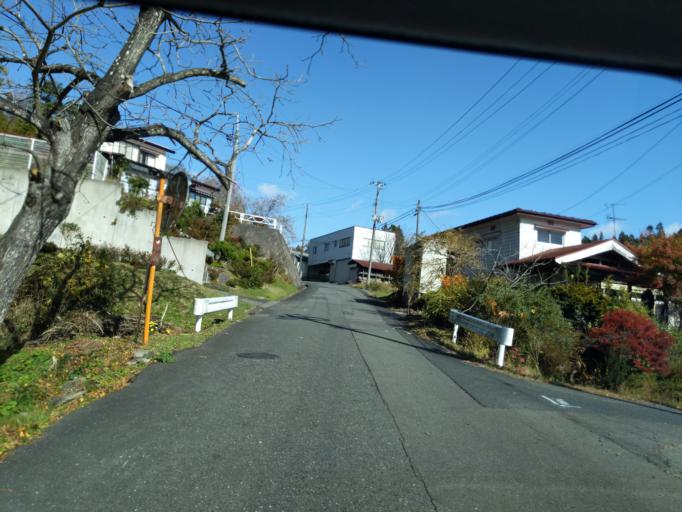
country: JP
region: Iwate
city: Ichinoseki
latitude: 39.0168
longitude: 141.1111
